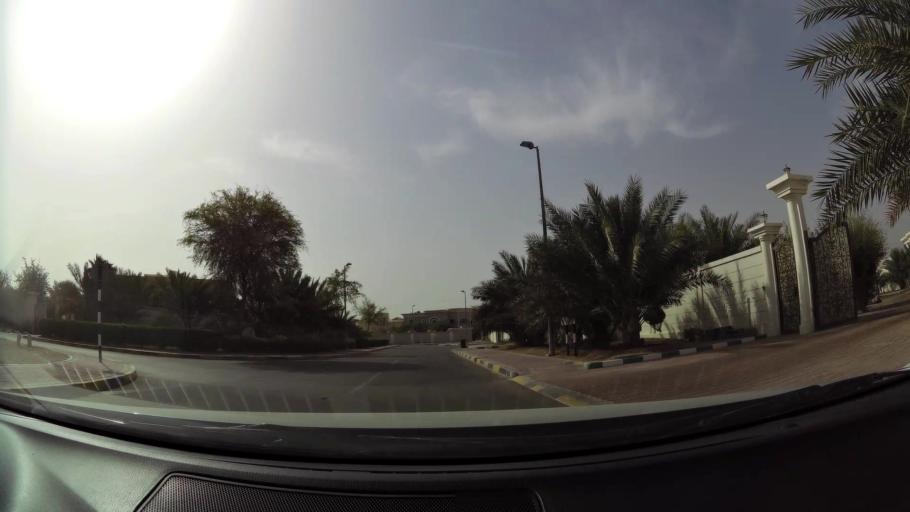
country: AE
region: Abu Dhabi
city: Al Ain
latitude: 24.1432
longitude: 55.7026
